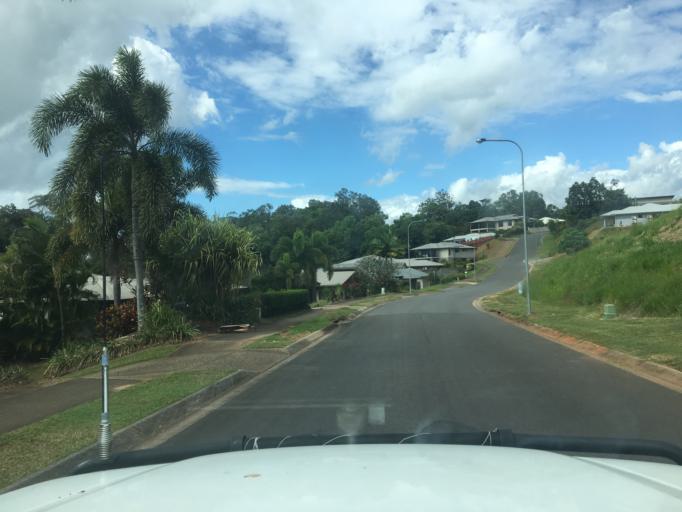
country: AU
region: Queensland
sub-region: Cairns
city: Woree
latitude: -16.9702
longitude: 145.7400
